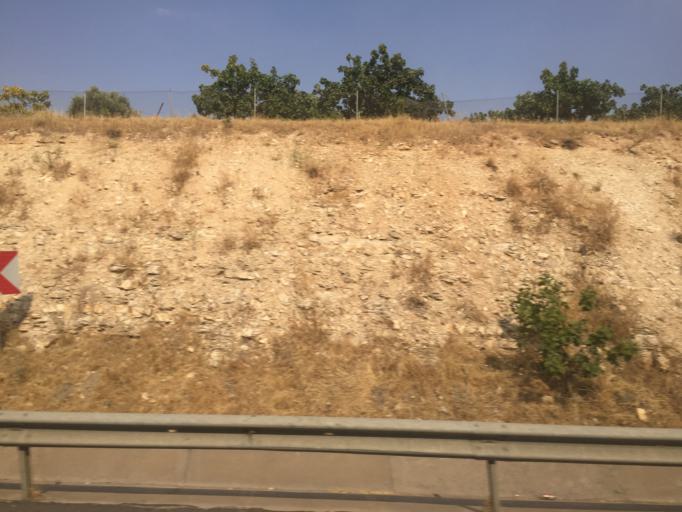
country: TR
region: Sanliurfa
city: Akziyaret
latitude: 37.2701
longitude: 38.8015
